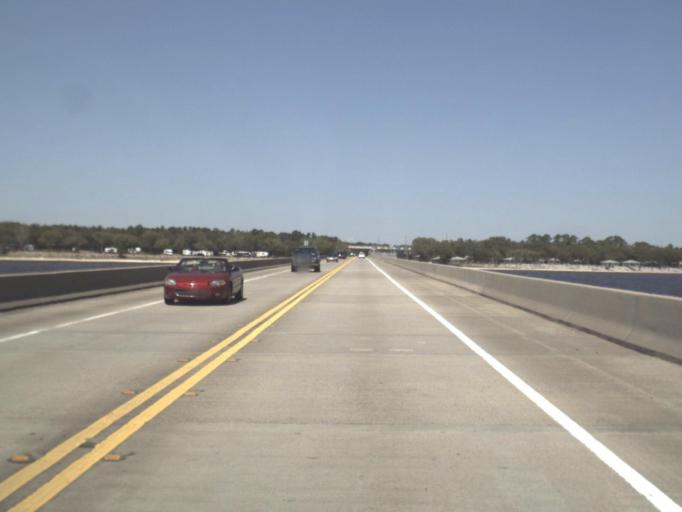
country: US
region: Florida
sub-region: Okaloosa County
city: Niceville
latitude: 30.4495
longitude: -86.4159
